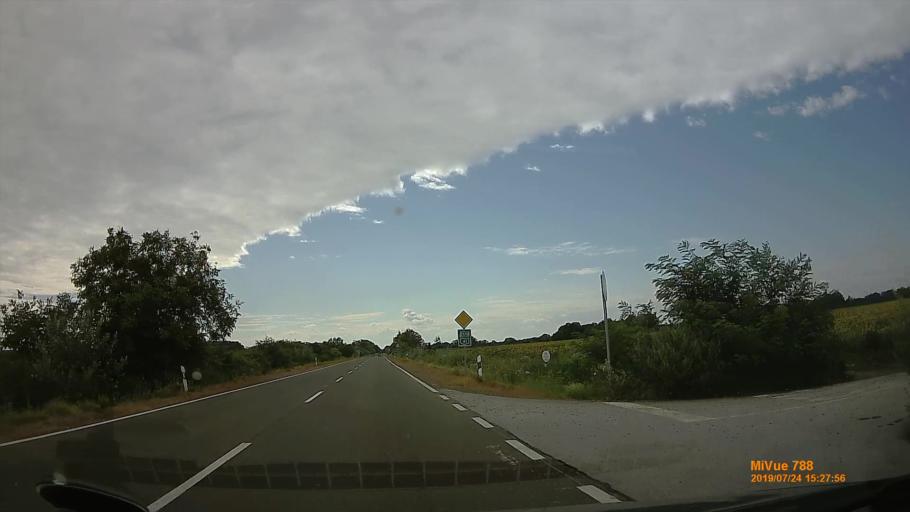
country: HU
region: Szabolcs-Szatmar-Bereg
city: Tarpa
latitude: 48.1608
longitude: 22.4891
